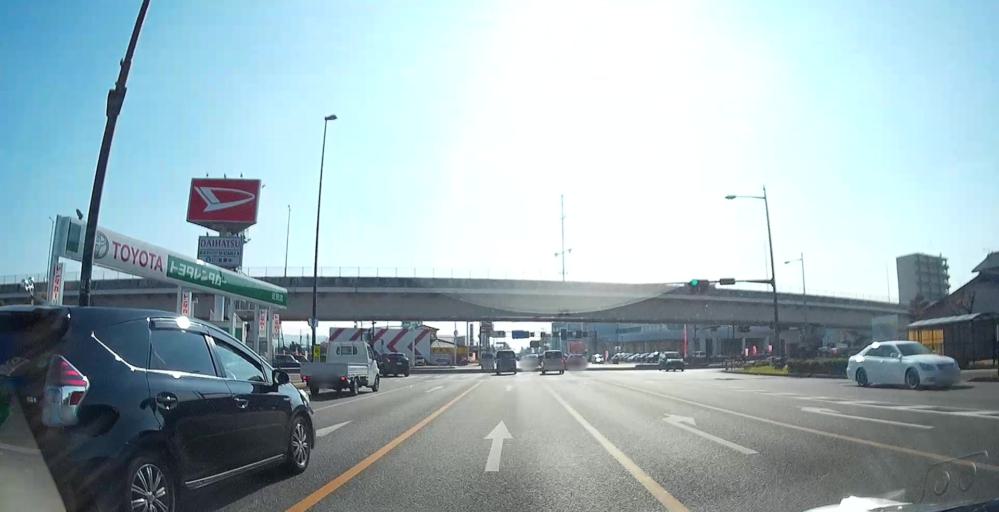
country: JP
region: Kumamoto
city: Kumamoto
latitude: 32.7629
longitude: 130.6898
